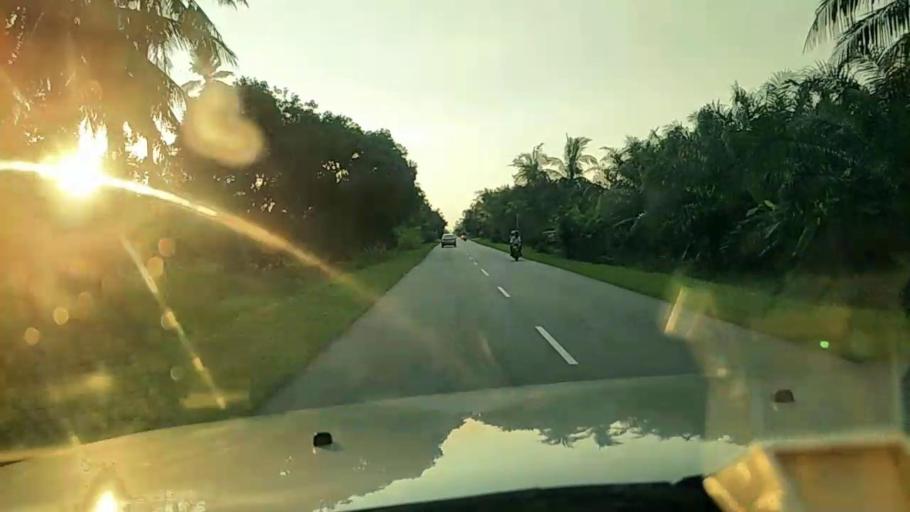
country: MY
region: Selangor
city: Kuala Selangor
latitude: 3.3067
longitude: 101.2933
